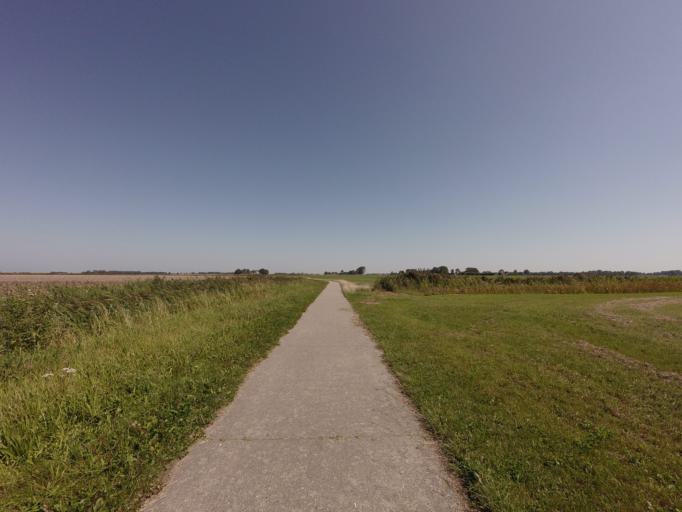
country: NL
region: Friesland
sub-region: Gemeente Dongeradeel
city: Anjum
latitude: 53.3855
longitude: 6.0627
